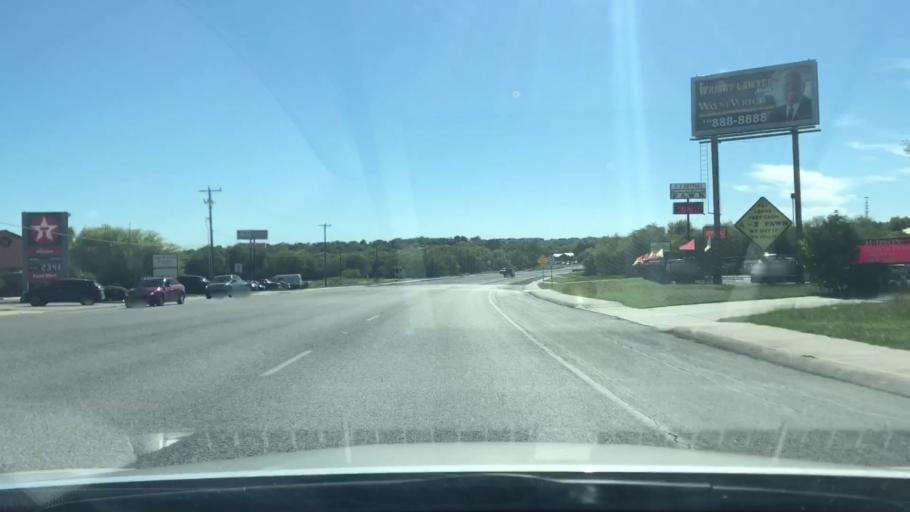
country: US
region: Texas
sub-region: Bexar County
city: Converse
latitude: 29.5077
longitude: -98.3093
